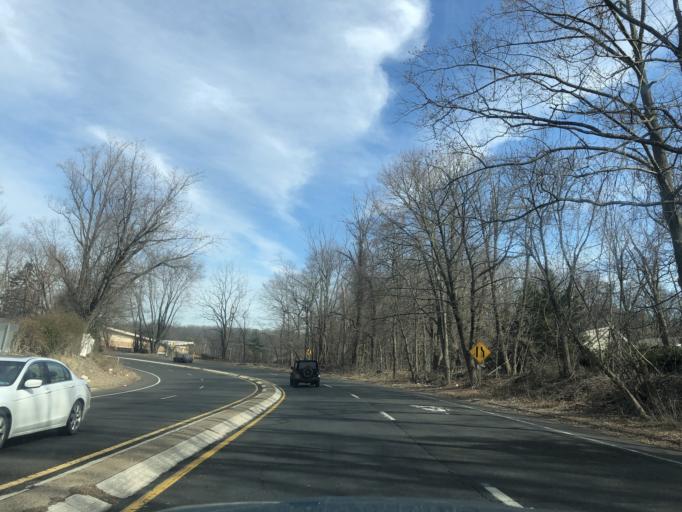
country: US
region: Pennsylvania
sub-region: Bucks County
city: Langhorne Manor
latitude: 40.1678
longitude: -74.9150
